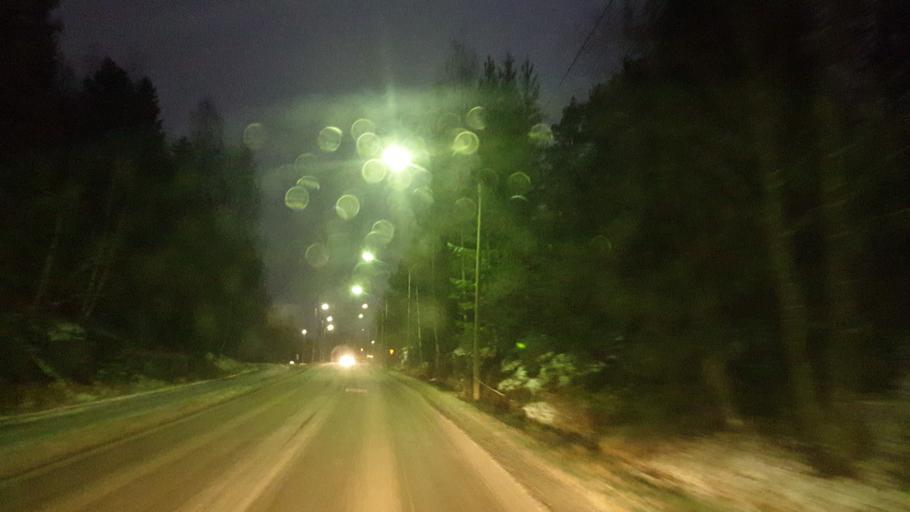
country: FI
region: Southern Savonia
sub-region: Savonlinna
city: Savonlinna
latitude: 61.8608
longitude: 28.9467
